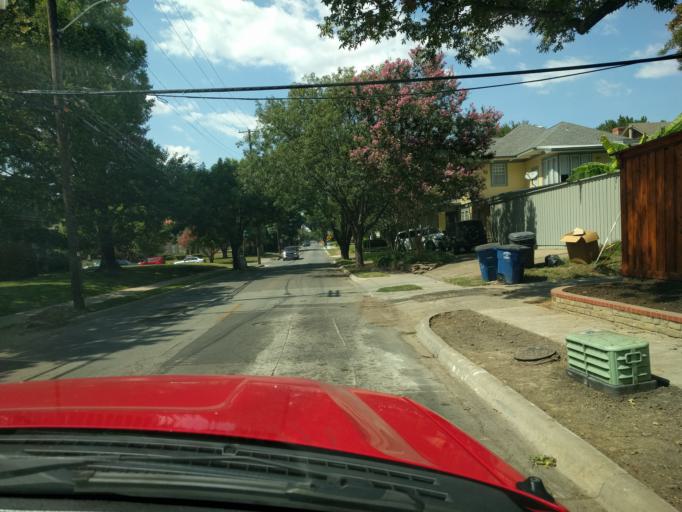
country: US
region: Texas
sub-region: Dallas County
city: Dallas
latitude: 32.7974
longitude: -96.7662
